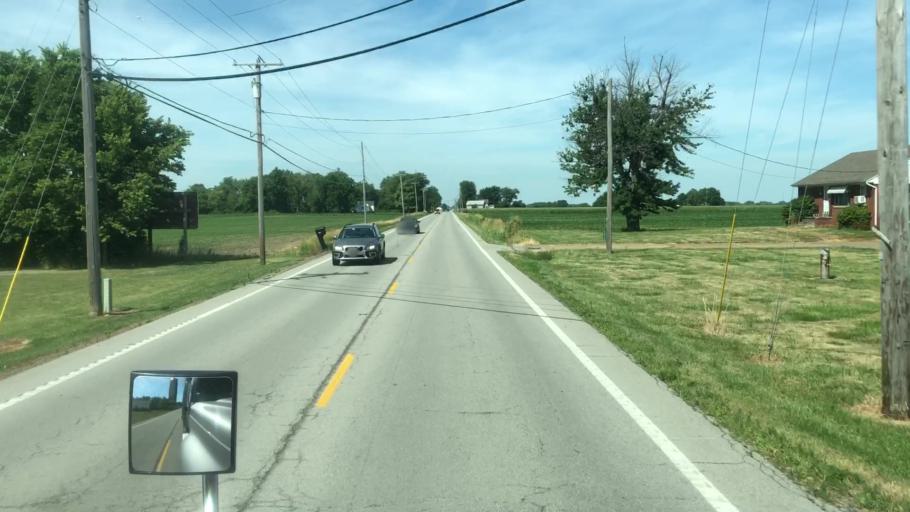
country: US
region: Ohio
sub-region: Ottawa County
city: Port Clinton
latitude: 41.4337
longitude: -82.8384
